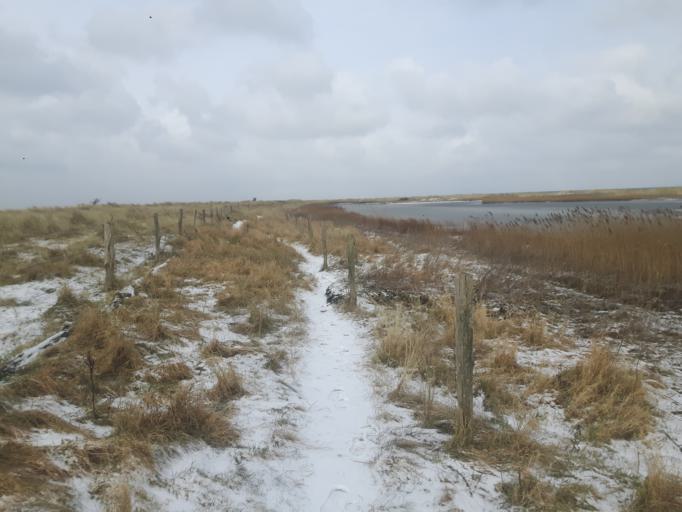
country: DE
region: Schleswig-Holstein
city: Fehmarn
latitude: 54.5119
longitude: 11.1899
